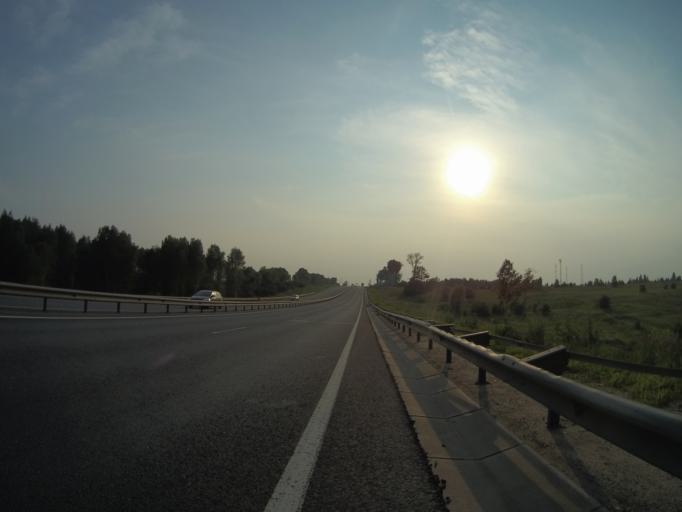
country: RU
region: Vladimir
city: Melekhovo
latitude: 56.2038
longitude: 41.1457
